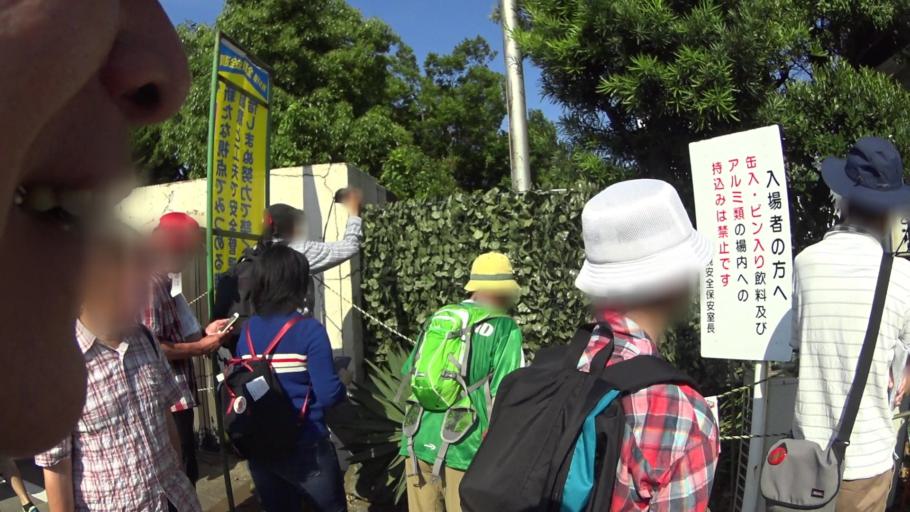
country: JP
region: Kanagawa
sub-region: Kawasaki-shi
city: Kawasaki
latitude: 35.4953
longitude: 139.6880
